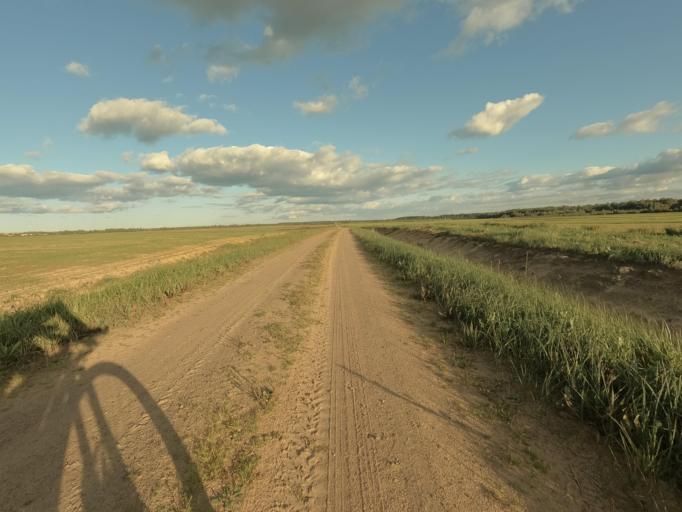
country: RU
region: Leningrad
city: Imeni Sverdlova
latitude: 59.8627
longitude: 30.7449
